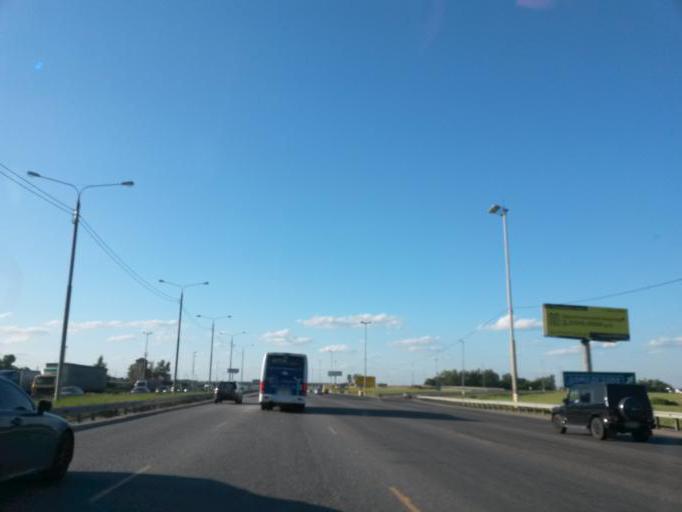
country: RU
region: Moskovskaya
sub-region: Podol'skiy Rayon
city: Podol'sk
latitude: 55.4326
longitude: 37.6149
